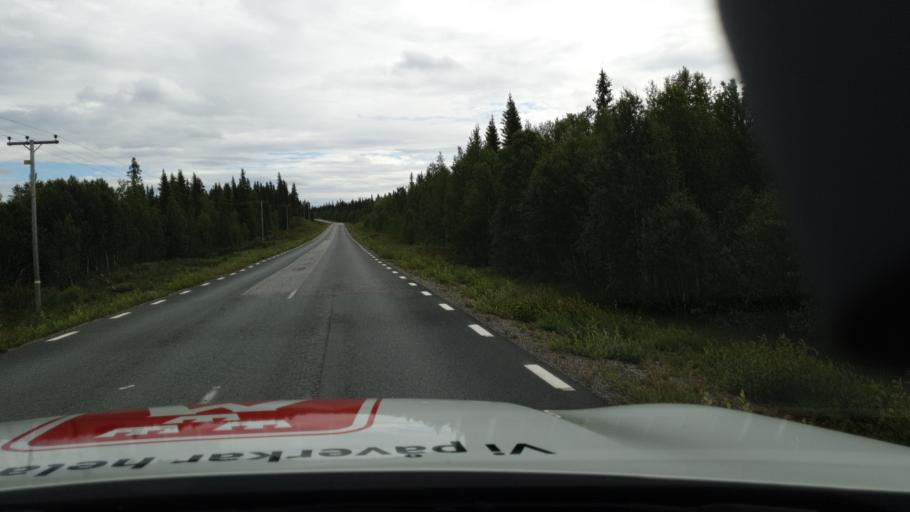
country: SE
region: Vaesterbotten
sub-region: Storumans Kommun
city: Fristad
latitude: 65.4218
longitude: 16.6139
